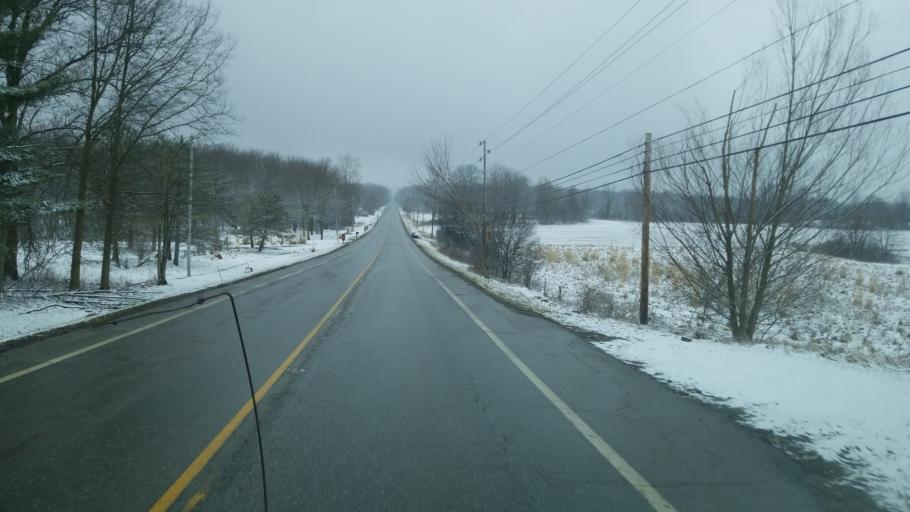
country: US
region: Ohio
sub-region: Portage County
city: Hiram
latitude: 41.3099
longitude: -81.1632
